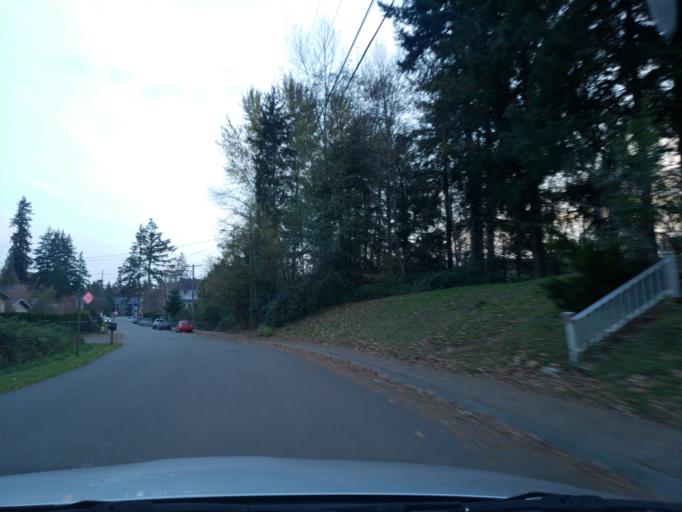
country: US
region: Washington
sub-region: King County
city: Kenmore
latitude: 47.7647
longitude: -122.2455
